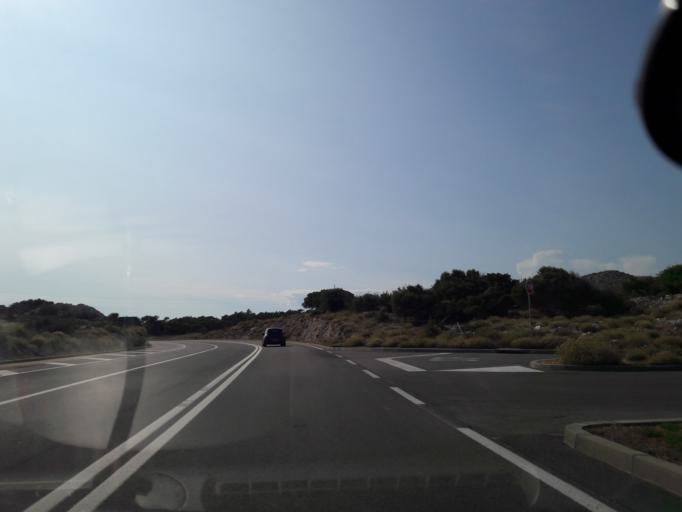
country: HR
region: Primorsko-Goranska
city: Banjol
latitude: 44.7057
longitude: 14.8441
